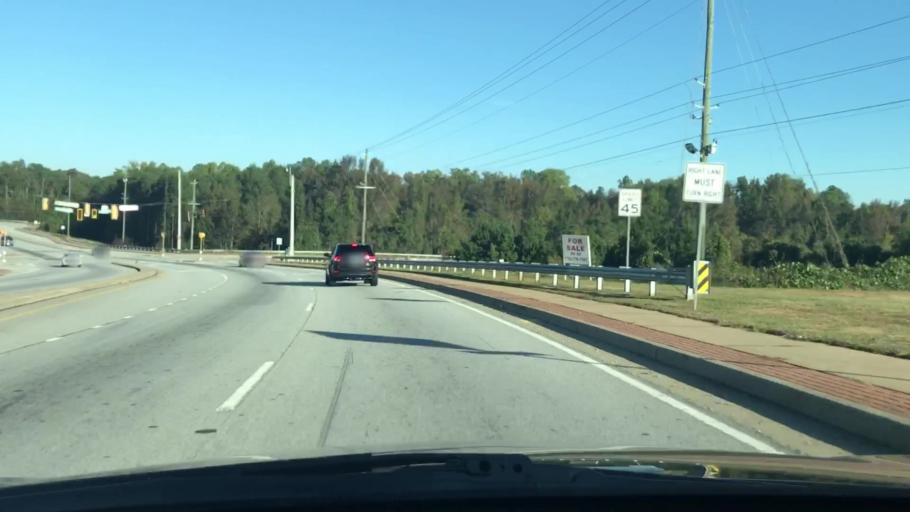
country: US
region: Georgia
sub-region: Douglas County
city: Douglasville
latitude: 33.7312
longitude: -84.7622
